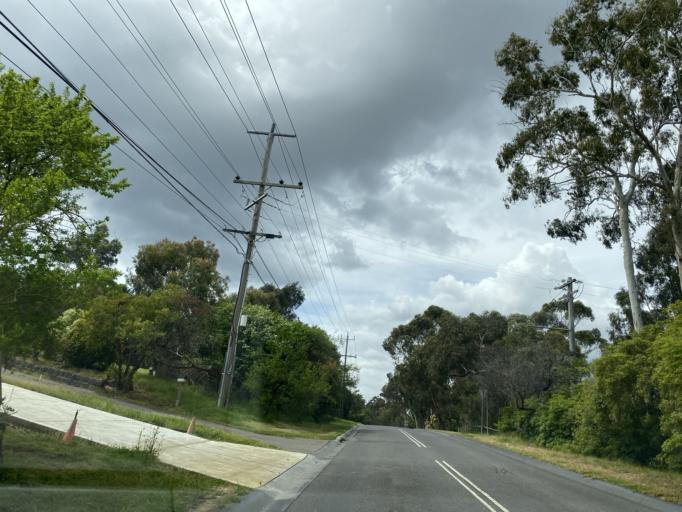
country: AU
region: Victoria
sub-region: Banyule
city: Lower Plenty
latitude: -37.7373
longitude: 145.1288
